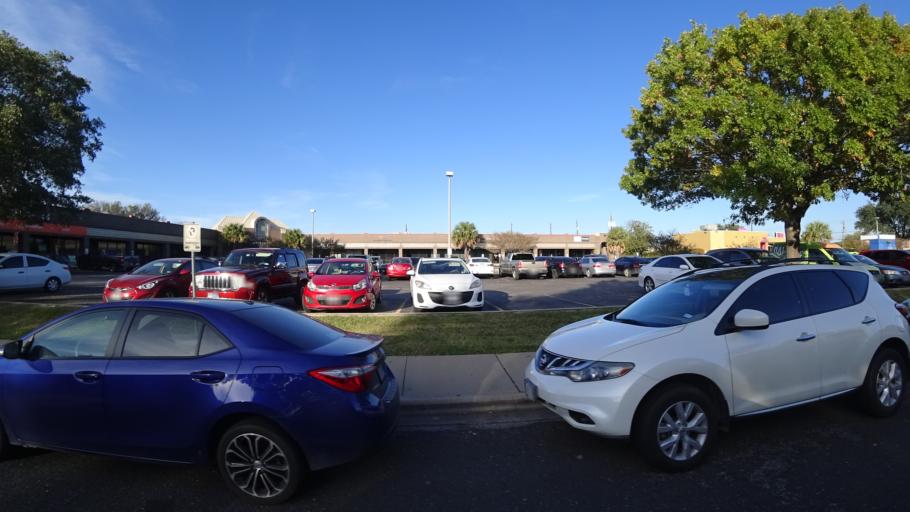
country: US
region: Texas
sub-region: Williamson County
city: Jollyville
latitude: 30.3687
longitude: -97.7290
